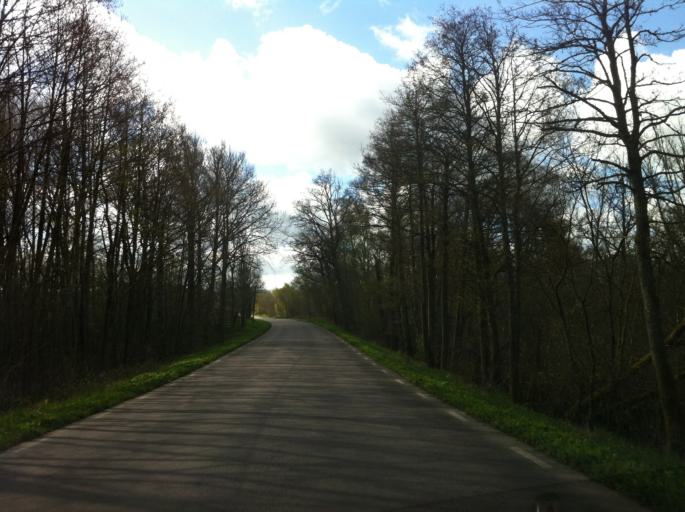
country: SE
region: Skane
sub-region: Horby Kommun
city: Hoerby
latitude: 55.8901
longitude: 13.6153
